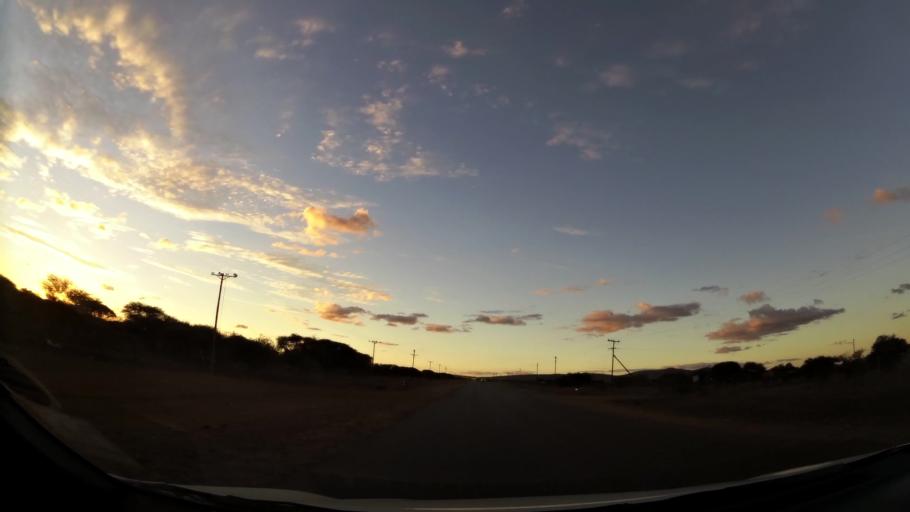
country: ZA
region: Limpopo
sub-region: Capricorn District Municipality
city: Polokwane
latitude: -23.7450
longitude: 29.4707
